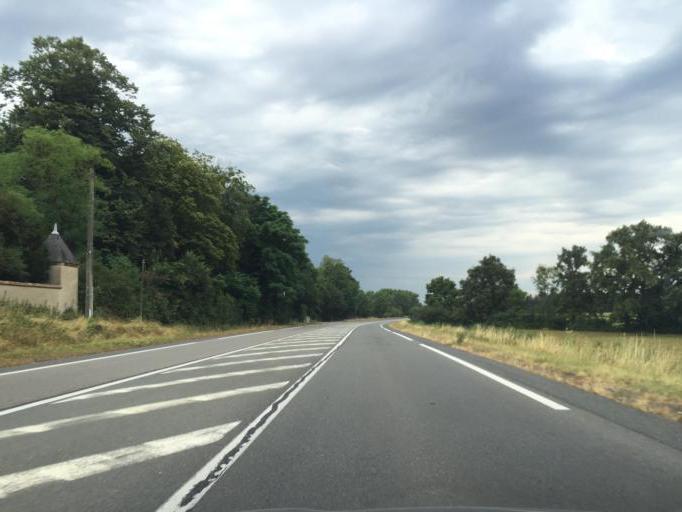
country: FR
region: Auvergne
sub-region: Departement de l'Allier
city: Bessay-sur-Allier
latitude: 46.4683
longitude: 3.3685
